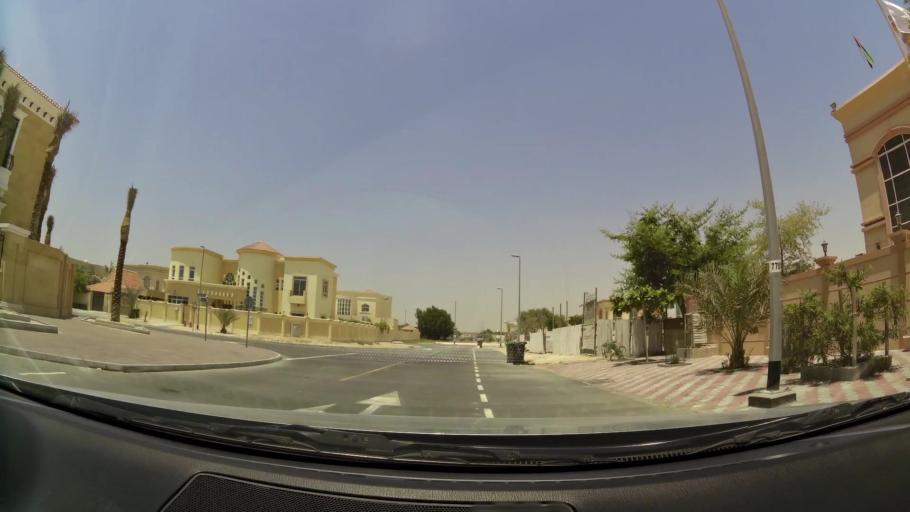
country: AE
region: Dubai
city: Dubai
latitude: 25.0907
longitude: 55.1998
